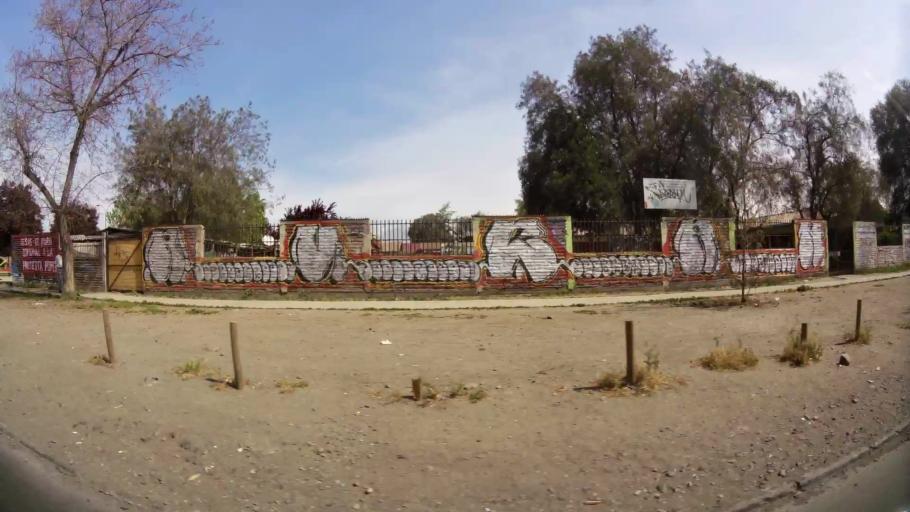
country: CL
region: Santiago Metropolitan
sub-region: Provincia de Santiago
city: Lo Prado
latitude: -33.4359
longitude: -70.7518
